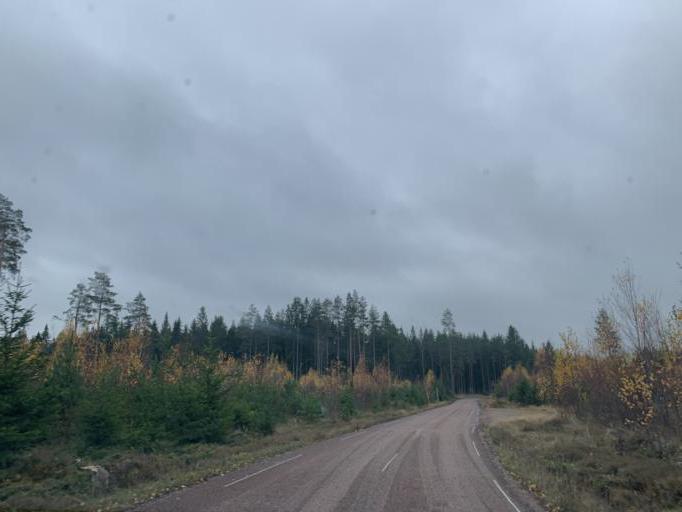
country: SE
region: Vaestmanland
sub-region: Surahammars Kommun
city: Surahammar
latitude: 59.6636
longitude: 16.0829
